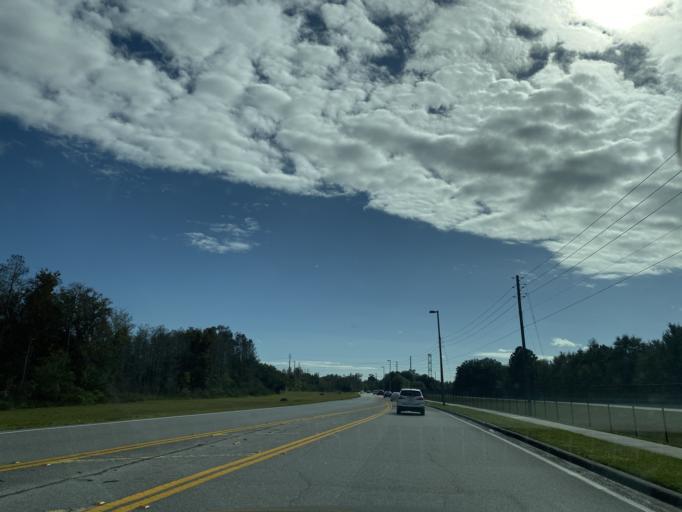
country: US
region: Florida
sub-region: Orange County
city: Azalea Park
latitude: 28.5065
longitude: -81.2564
